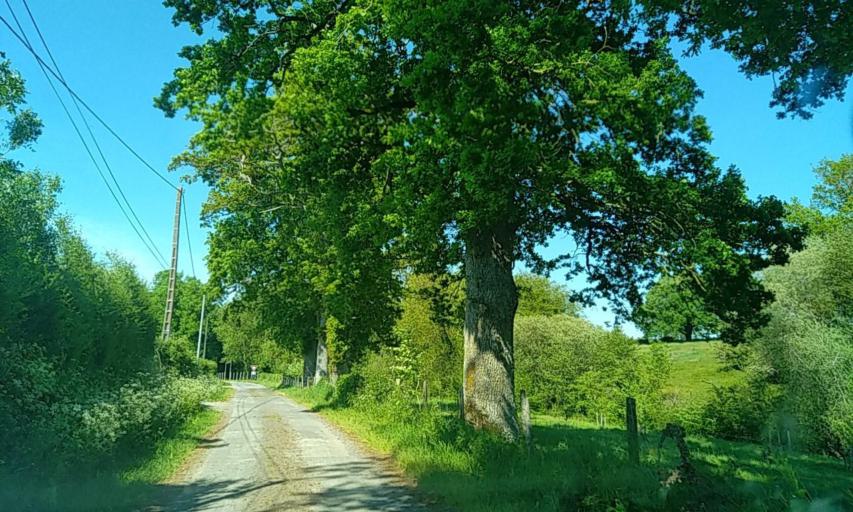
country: FR
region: Poitou-Charentes
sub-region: Departement des Deux-Sevres
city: Boisme
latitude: 46.7673
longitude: -0.4452
